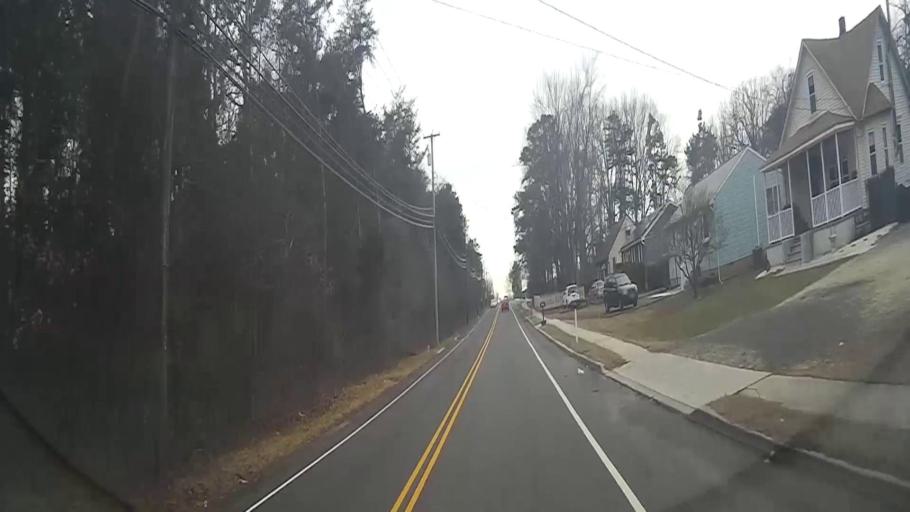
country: US
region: New Jersey
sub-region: Camden County
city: Pine Hill
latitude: 39.7760
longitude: -74.9601
